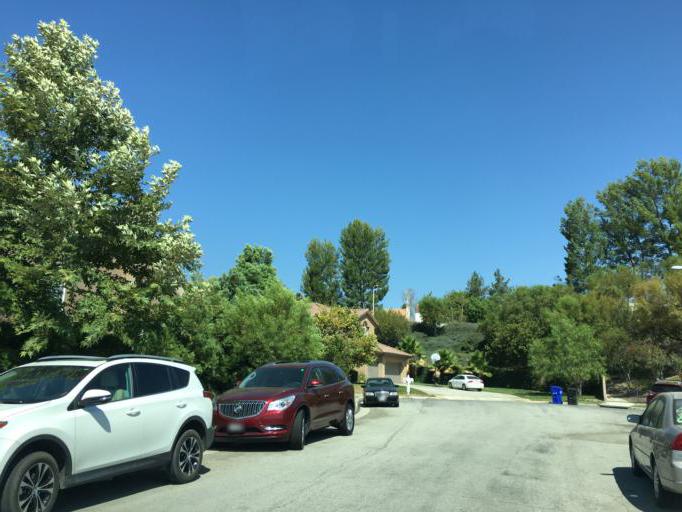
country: US
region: California
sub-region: Los Angeles County
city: Santa Clarita
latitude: 34.3826
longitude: -118.5822
